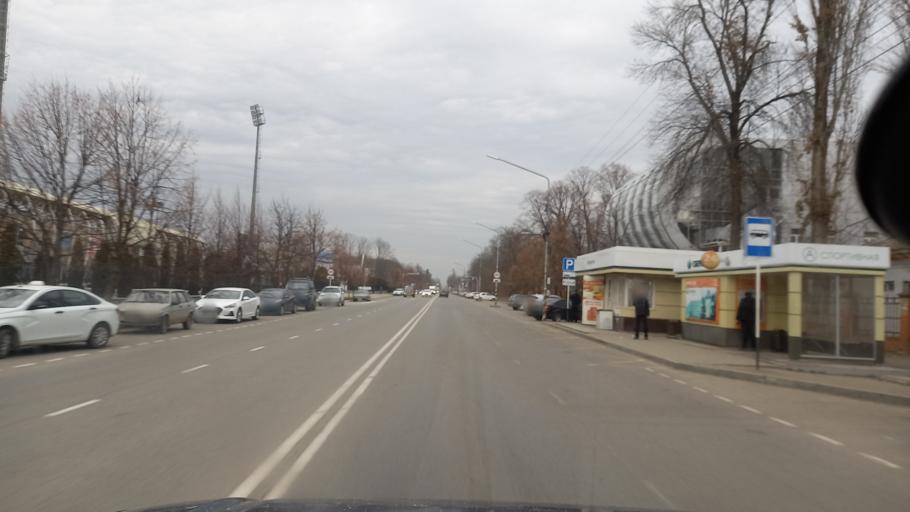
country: RU
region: Adygeya
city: Maykop
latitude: 44.5947
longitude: 40.1088
